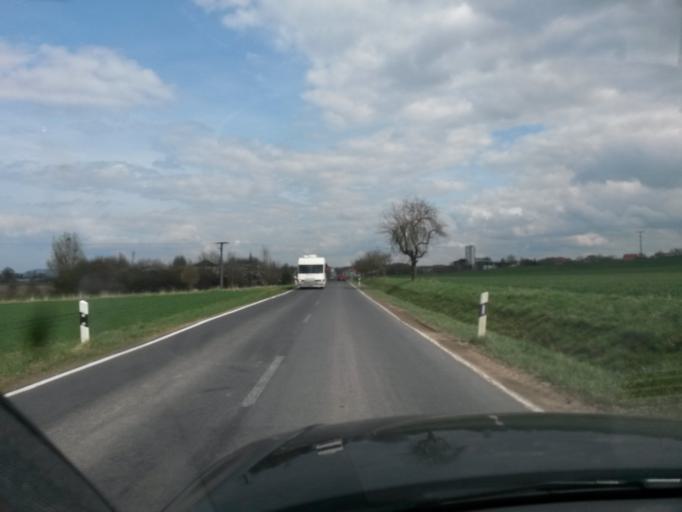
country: DE
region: Bavaria
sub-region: Regierungsbezirk Unterfranken
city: Frankenwinheim
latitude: 49.8847
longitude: 10.3027
